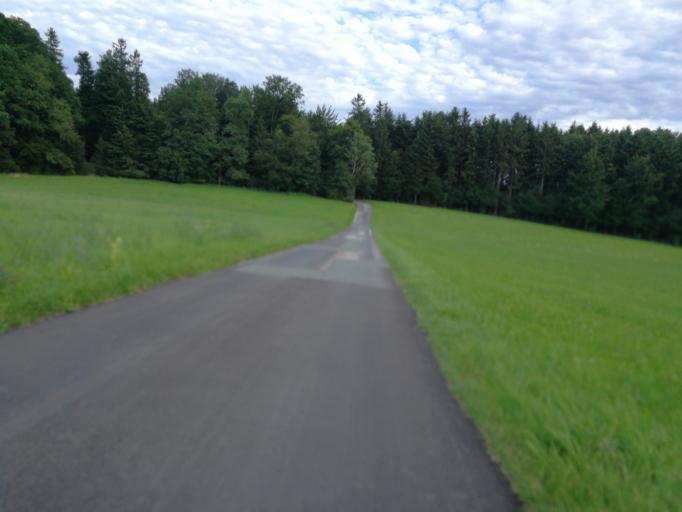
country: AT
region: Salzburg
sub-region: Politischer Bezirk Salzburg-Umgebung
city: Anthering
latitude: 47.8822
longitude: 13.0333
